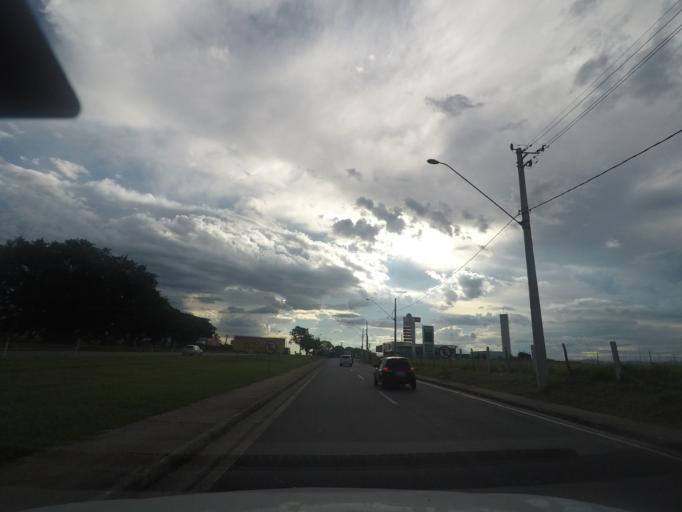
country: BR
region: Sao Paulo
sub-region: Taubate
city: Taubate
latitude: -23.0498
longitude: -45.6013
